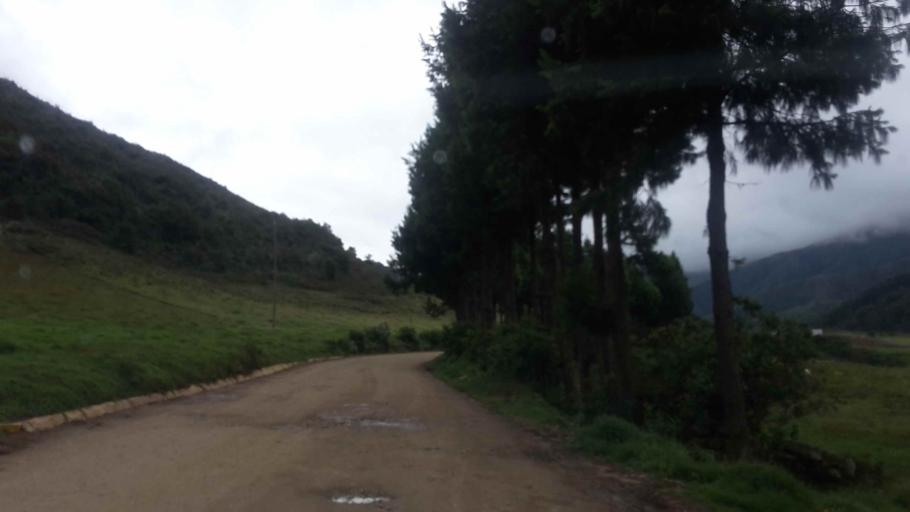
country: BO
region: Cochabamba
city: Totora
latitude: -17.5756
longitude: -65.2872
